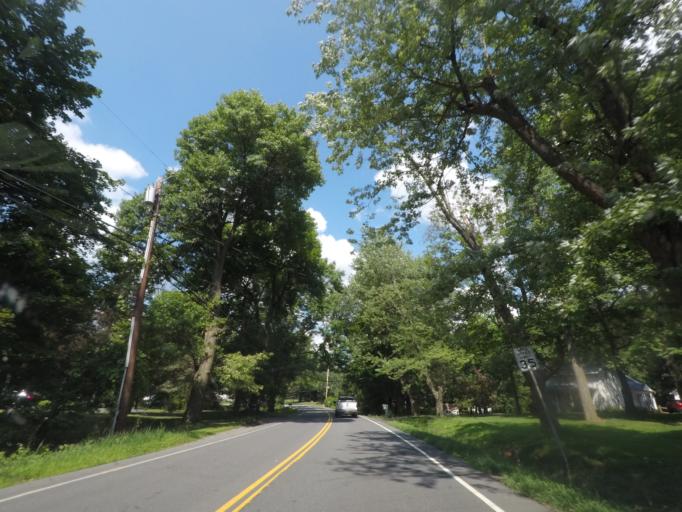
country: US
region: New York
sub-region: Rensselaer County
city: Wynantskill
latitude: 42.6808
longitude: -73.6760
